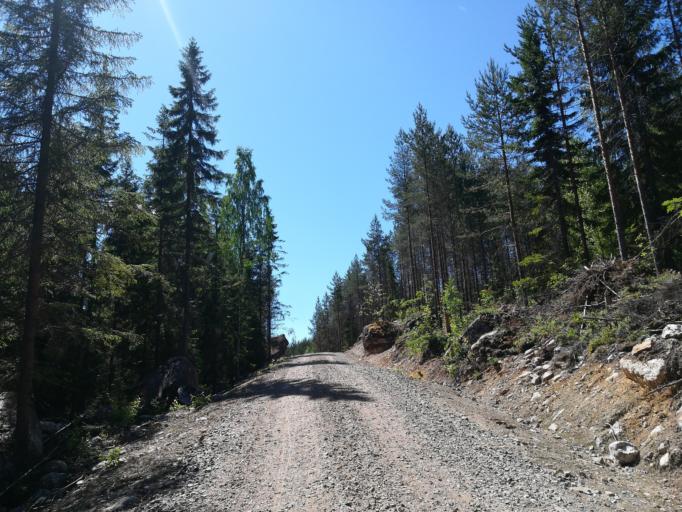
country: FI
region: Southern Savonia
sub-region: Mikkeli
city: Puumala
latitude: 61.6170
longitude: 28.1714
